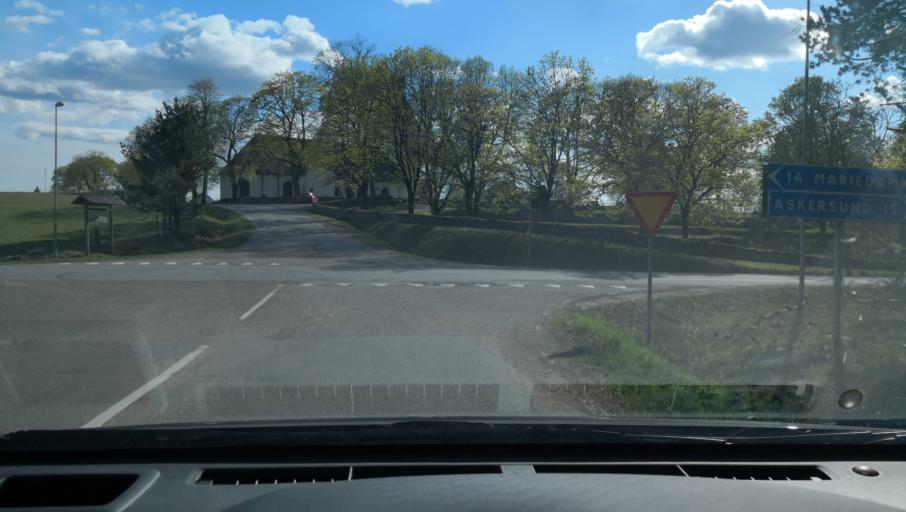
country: SE
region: OErebro
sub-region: Askersunds Kommun
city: Asbro
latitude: 58.9583
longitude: 15.0615
